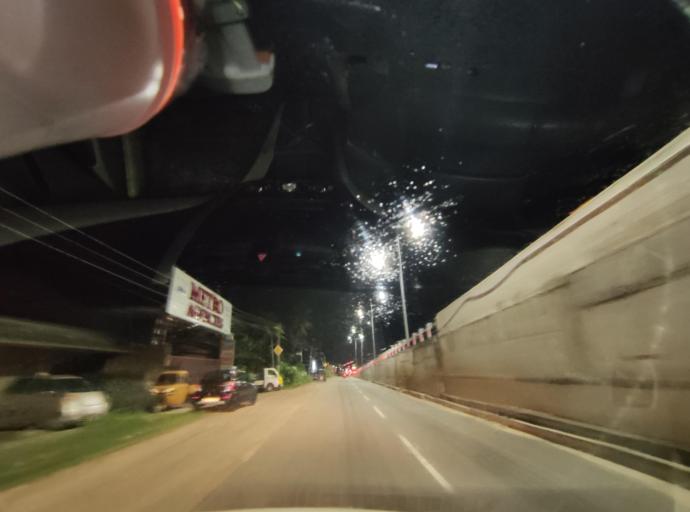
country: IN
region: Kerala
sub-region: Thiruvananthapuram
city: Thiruvananthapuram
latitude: 8.4848
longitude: 76.9298
